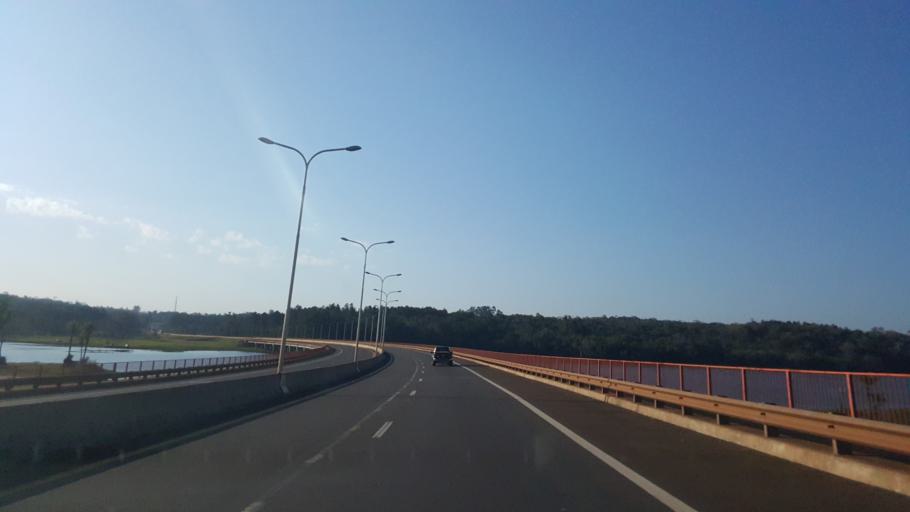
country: AR
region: Misiones
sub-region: Departamento de San Ignacio
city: San Ignacio
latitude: -27.2882
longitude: -55.5329
